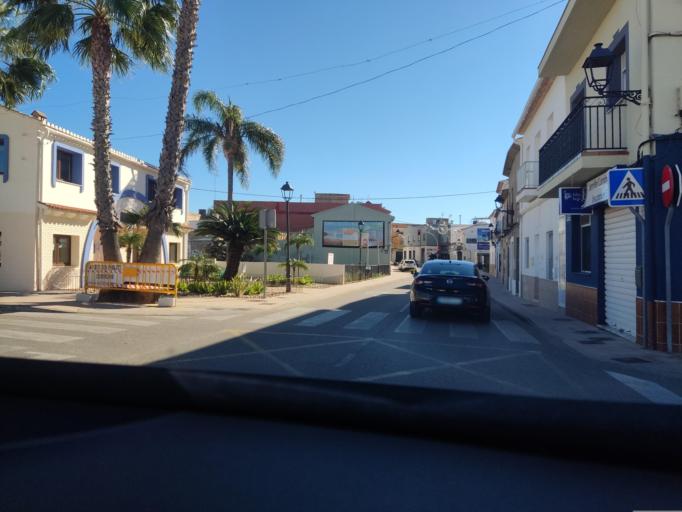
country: ES
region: Valencia
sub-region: Provincia de Alicante
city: els Poblets
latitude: 38.8500
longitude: 0.0182
